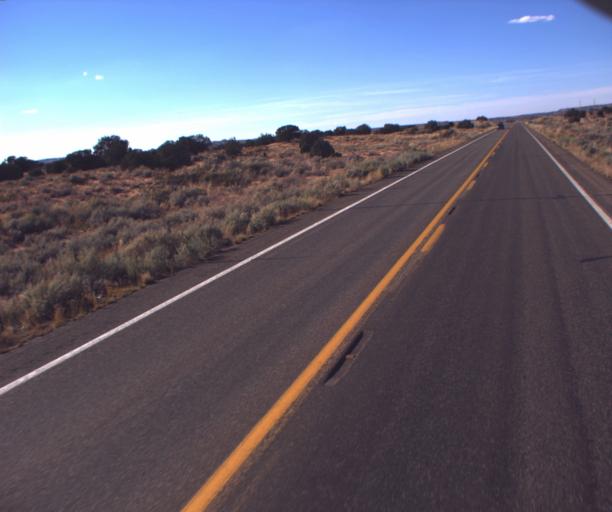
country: US
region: Arizona
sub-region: Coconino County
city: Kaibito
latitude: 36.5949
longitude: -111.1630
